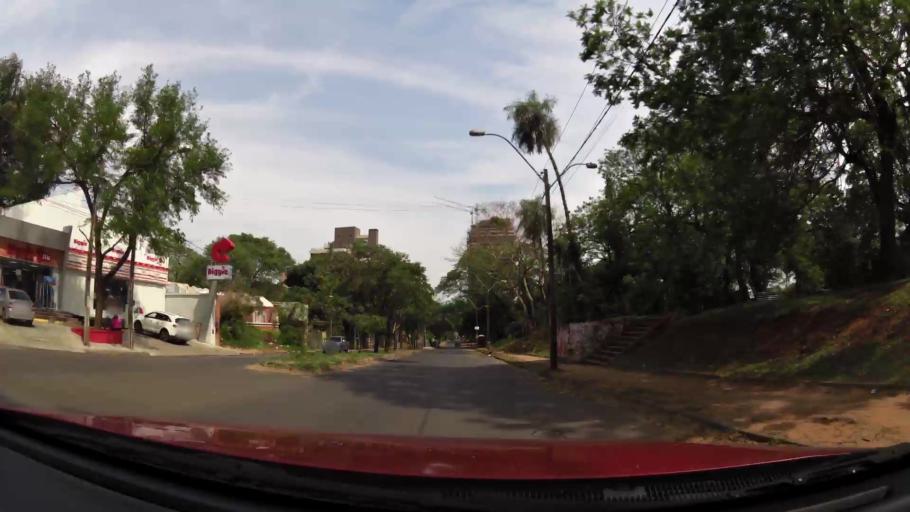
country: PY
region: Asuncion
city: Asuncion
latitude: -25.2646
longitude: -57.5711
